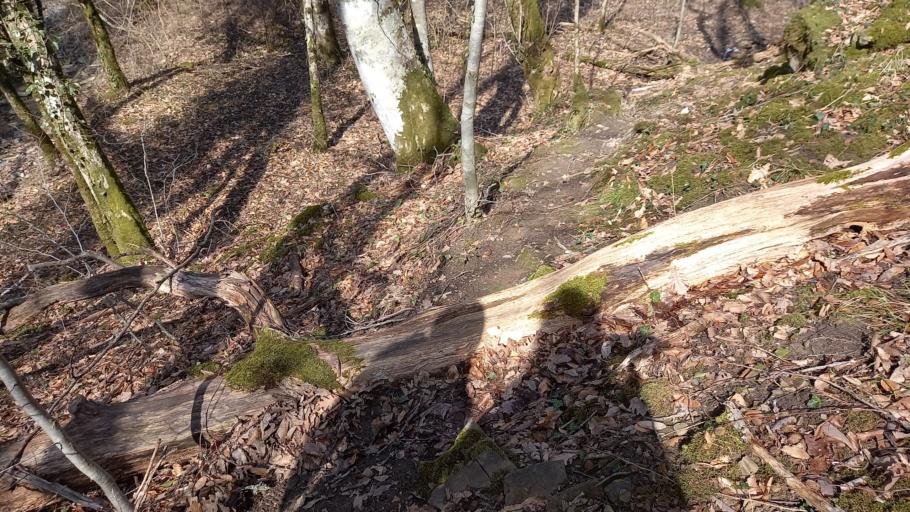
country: RU
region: Krasnodarskiy
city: Arkhipo-Osipovka
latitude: 44.3830
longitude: 38.6024
